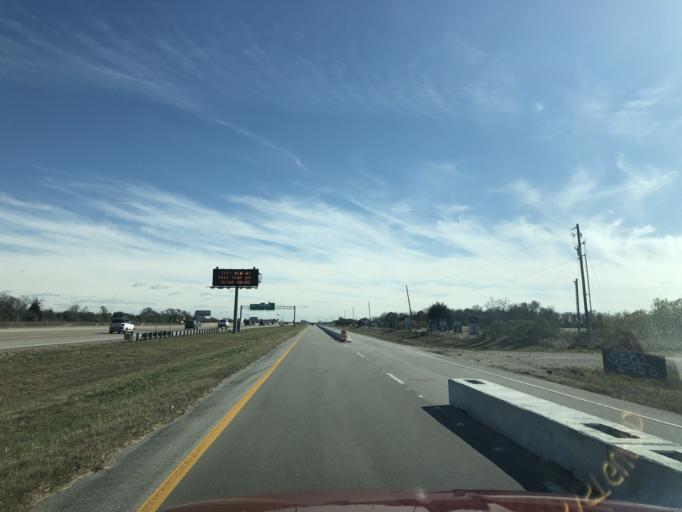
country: US
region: Texas
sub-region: Galveston County
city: Dickinson
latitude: 29.4233
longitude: -95.0537
